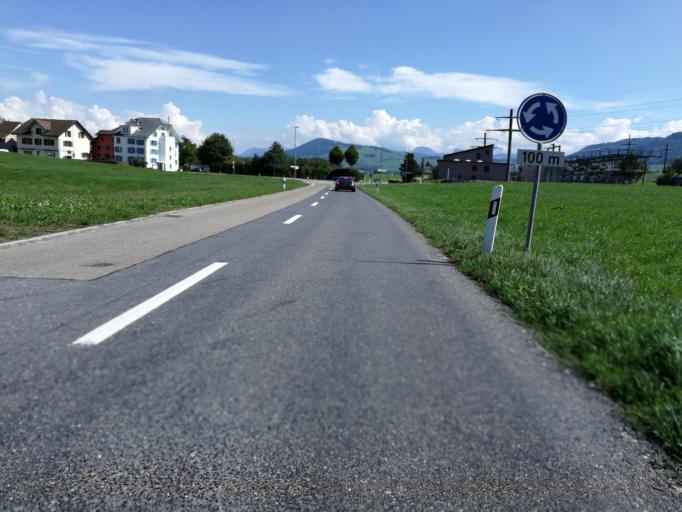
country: CH
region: Zurich
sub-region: Bezirk Horgen
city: Waedenswil / Eichweid
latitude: 47.2073
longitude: 8.6614
